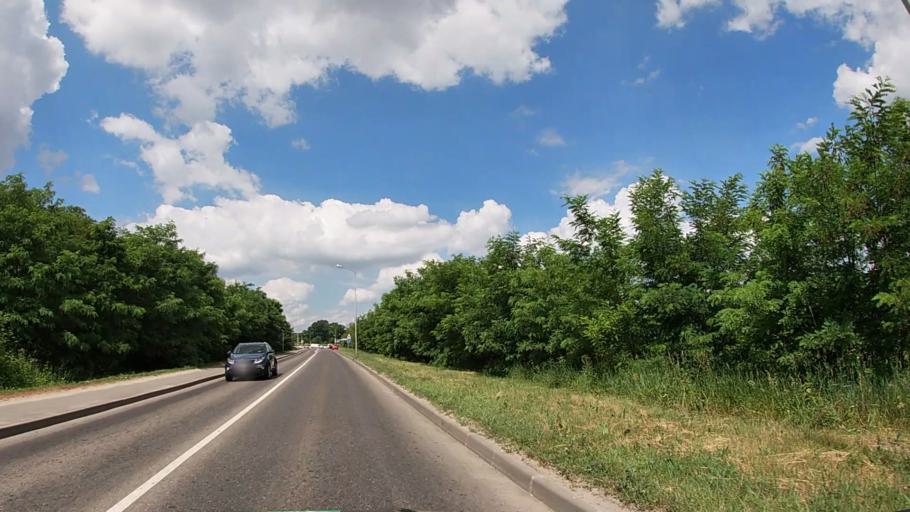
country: RU
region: Belgorod
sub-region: Belgorodskiy Rayon
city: Belgorod
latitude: 50.5944
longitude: 36.5558
